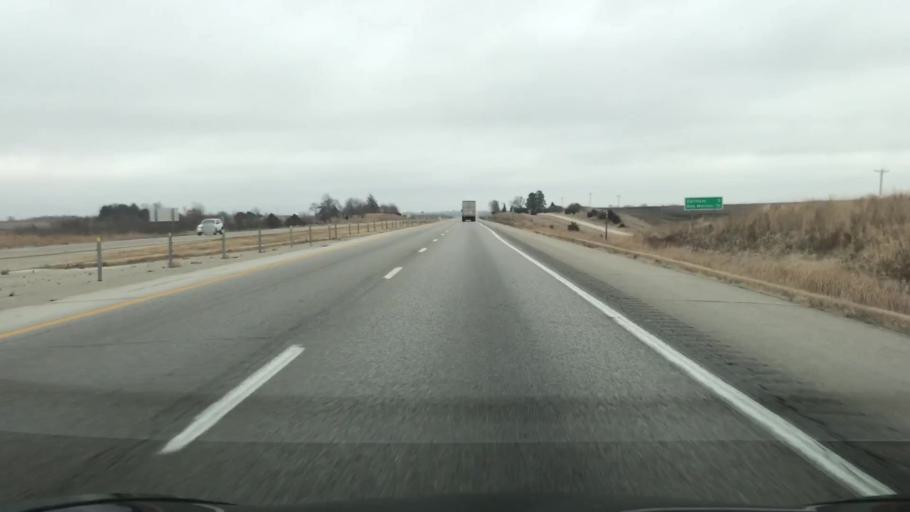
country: US
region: Iowa
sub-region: Madison County
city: Earlham
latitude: 41.5178
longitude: -94.1834
